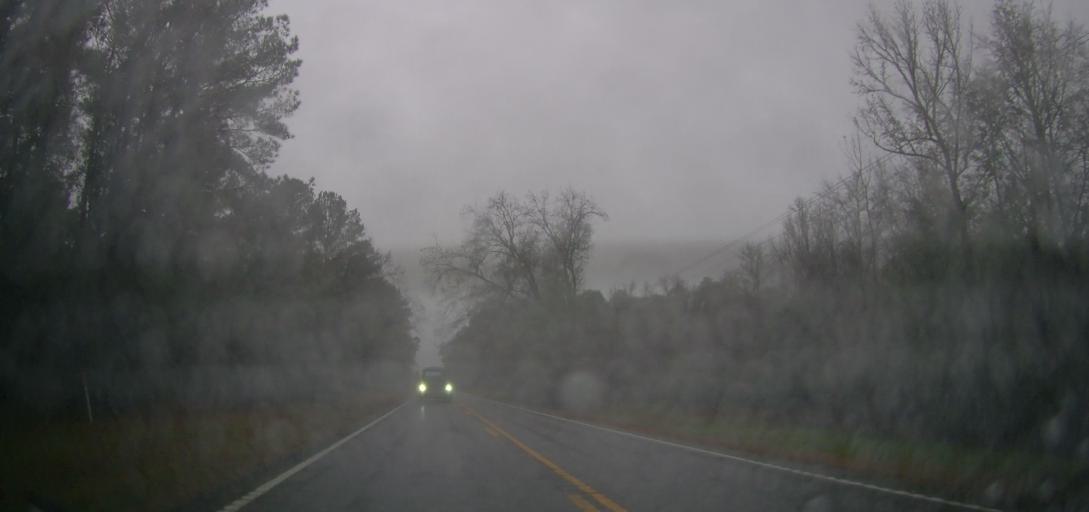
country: US
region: Georgia
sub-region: Jones County
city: Gray
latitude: 33.1482
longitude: -83.4613
